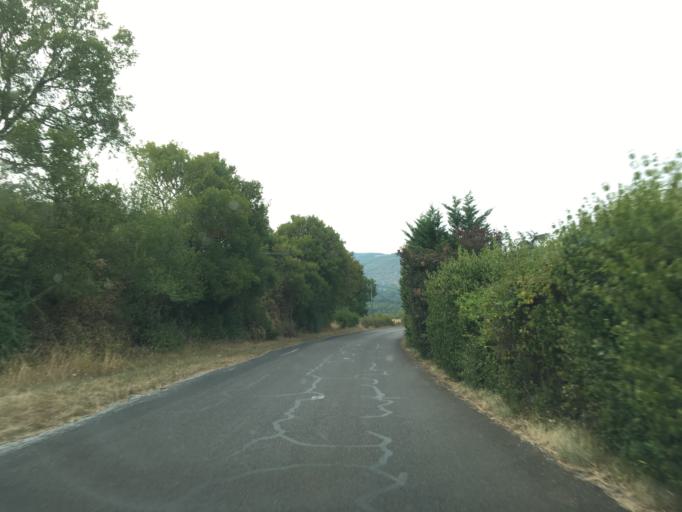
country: FR
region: Midi-Pyrenees
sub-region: Departement du Lot
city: Souillac
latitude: 44.8404
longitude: 1.5585
